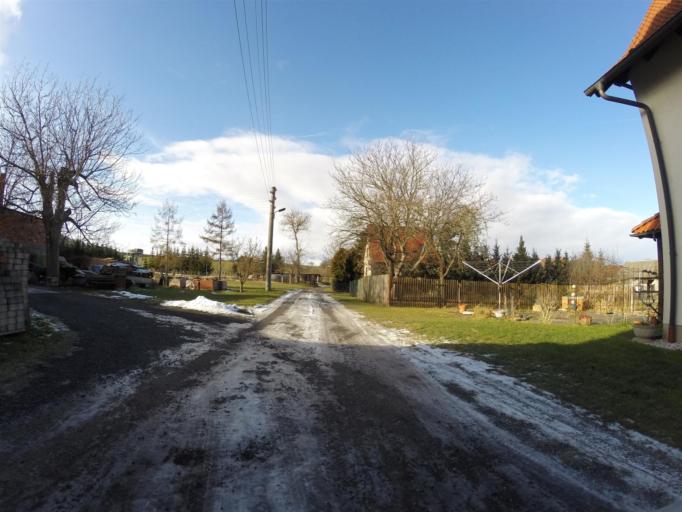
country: DE
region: Thuringia
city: Nausnitz
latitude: 50.9345
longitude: 11.7173
